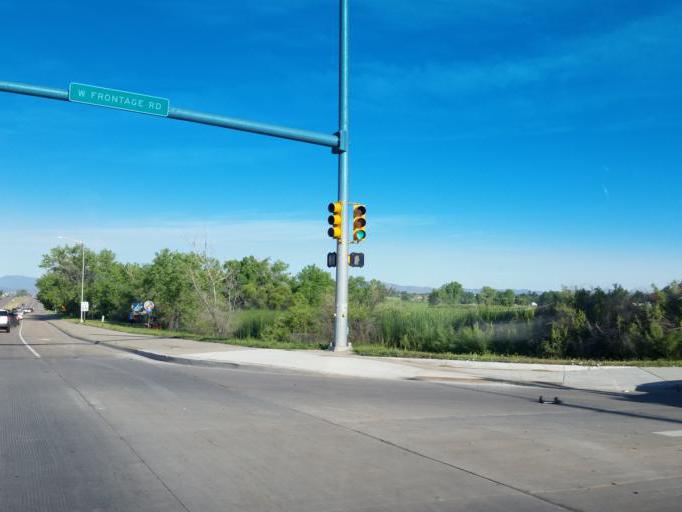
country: US
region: Colorado
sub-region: Weld County
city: Windsor
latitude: 40.5235
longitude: -104.9974
